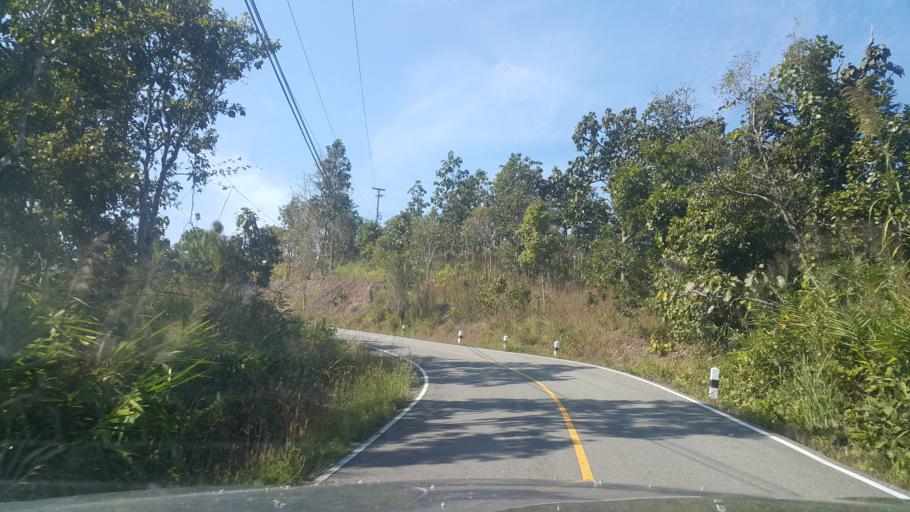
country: TH
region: Chiang Mai
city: Samoeng
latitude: 18.8975
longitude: 98.6778
